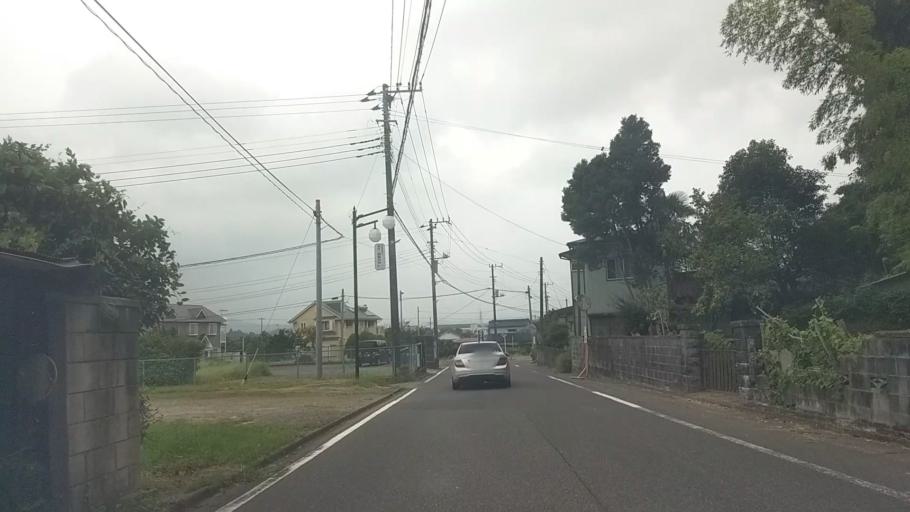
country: JP
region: Chiba
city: Futtsu
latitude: 35.2186
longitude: 139.8778
